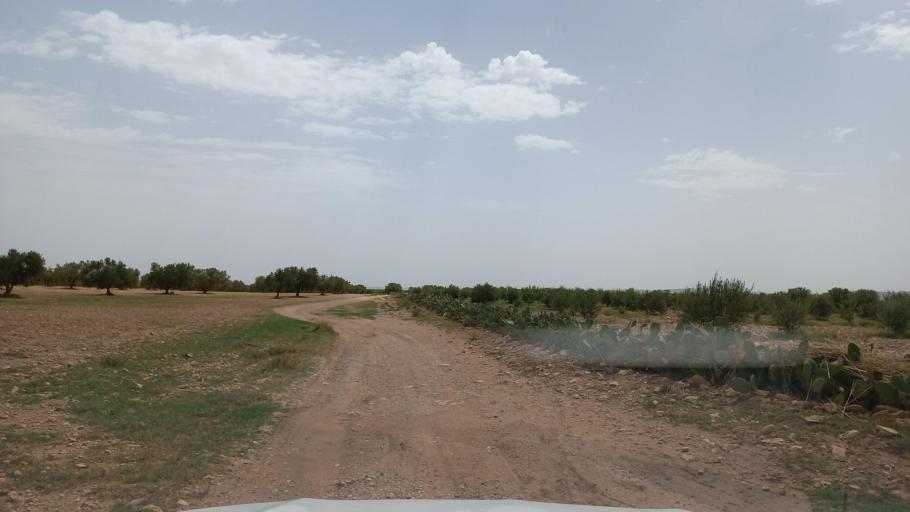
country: TN
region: Al Qasrayn
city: Kasserine
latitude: 35.2934
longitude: 9.0189
